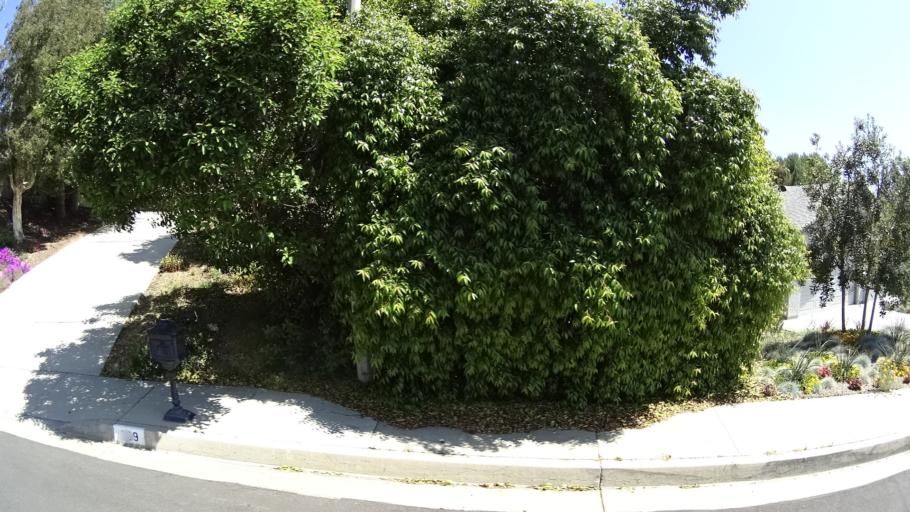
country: US
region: California
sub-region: Ventura County
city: Casa Conejo
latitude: 34.2013
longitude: -118.8932
